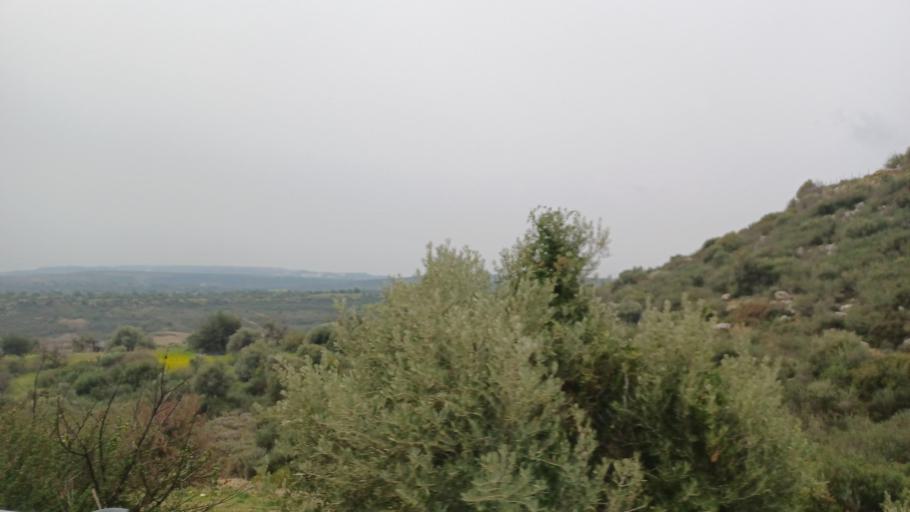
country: CY
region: Limassol
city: Pissouri
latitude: 34.7236
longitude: 32.7364
